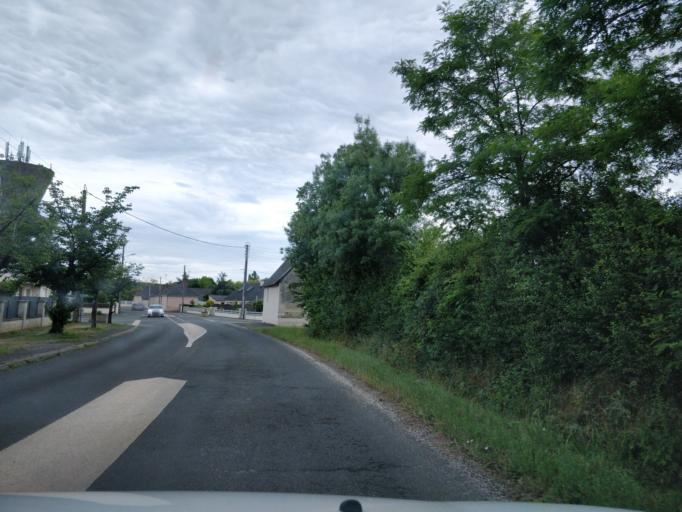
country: FR
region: Pays de la Loire
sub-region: Departement de Maine-et-Loire
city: Feneu
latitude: 47.5745
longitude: -0.5963
